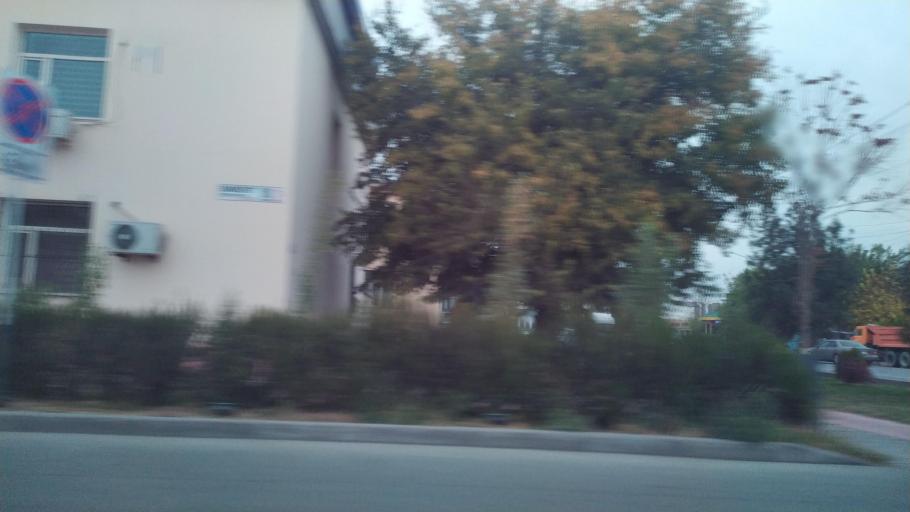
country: KZ
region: Ongtustik Qazaqstan
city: Turkestan
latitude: 43.2996
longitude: 68.2765
